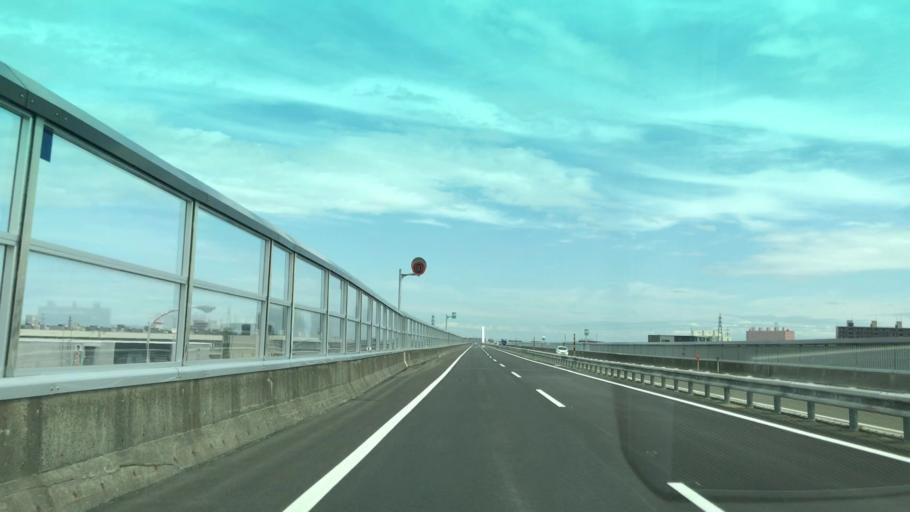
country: JP
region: Hokkaido
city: Sapporo
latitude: 43.0948
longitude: 141.2896
